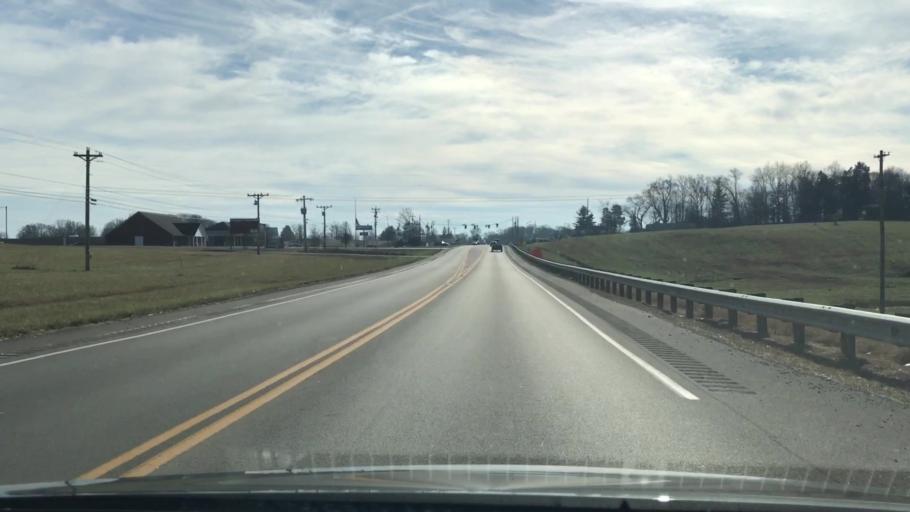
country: US
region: Kentucky
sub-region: Monroe County
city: Tompkinsville
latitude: 36.7273
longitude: -85.6875
